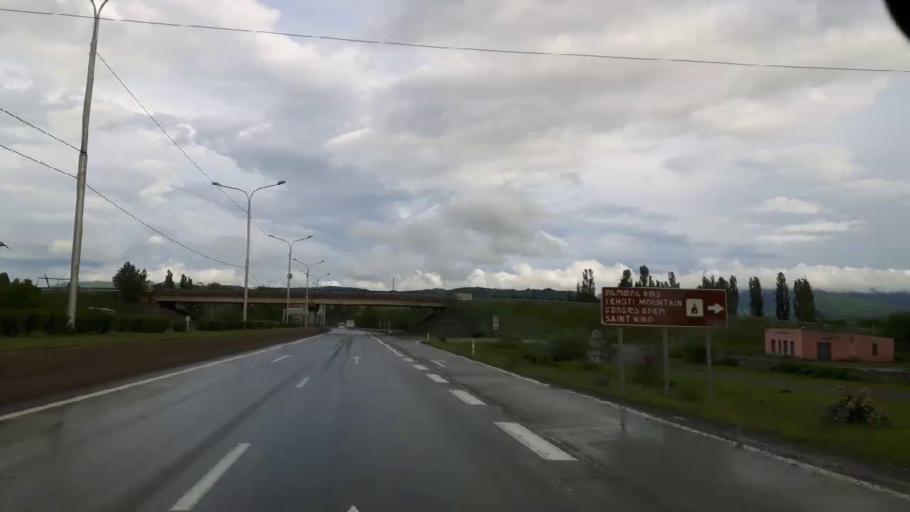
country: GE
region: Shida Kartli
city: Kaspi
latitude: 41.9139
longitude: 44.5590
